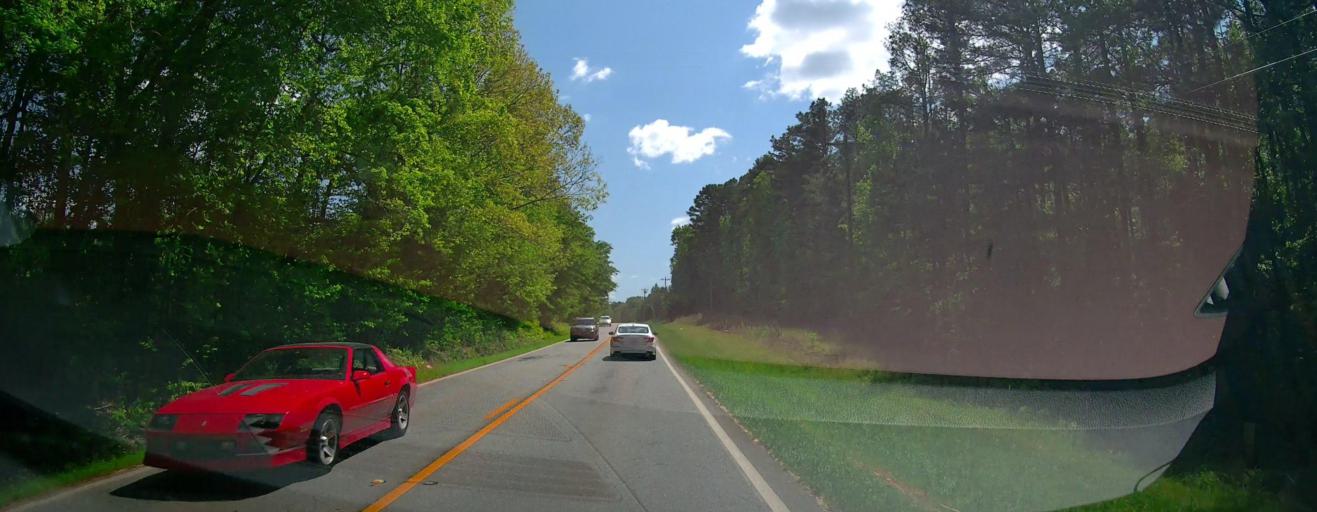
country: US
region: Georgia
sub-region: Putnam County
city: Eatonton
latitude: 33.3176
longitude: -83.2987
